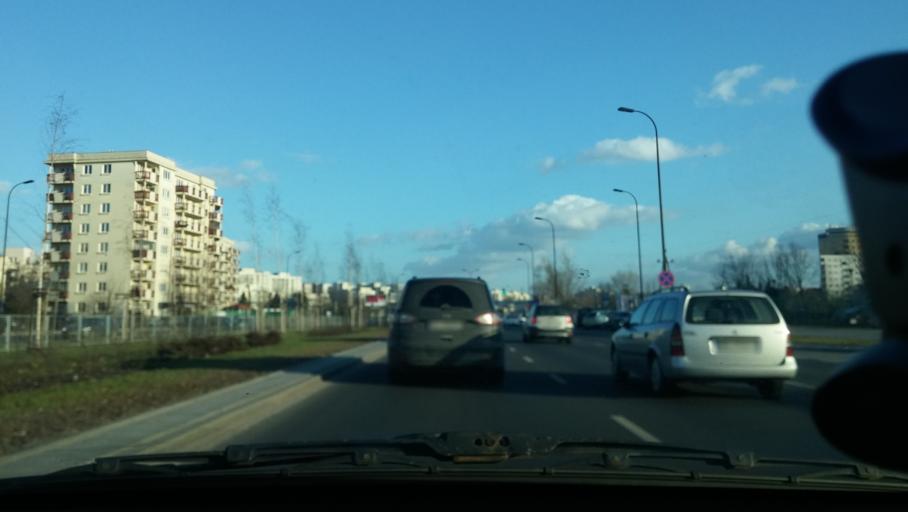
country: PL
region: Masovian Voivodeship
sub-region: Warszawa
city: Ursynow
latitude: 52.1488
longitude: 21.0337
